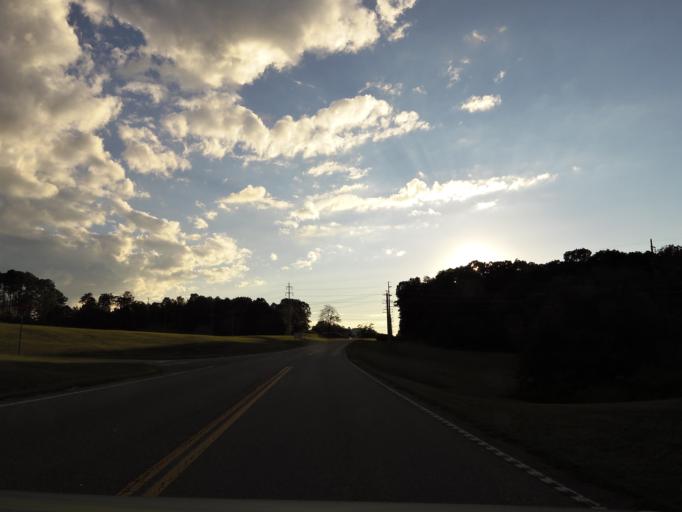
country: US
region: Tennessee
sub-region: Jefferson County
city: Jefferson City
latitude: 36.1578
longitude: -83.5124
